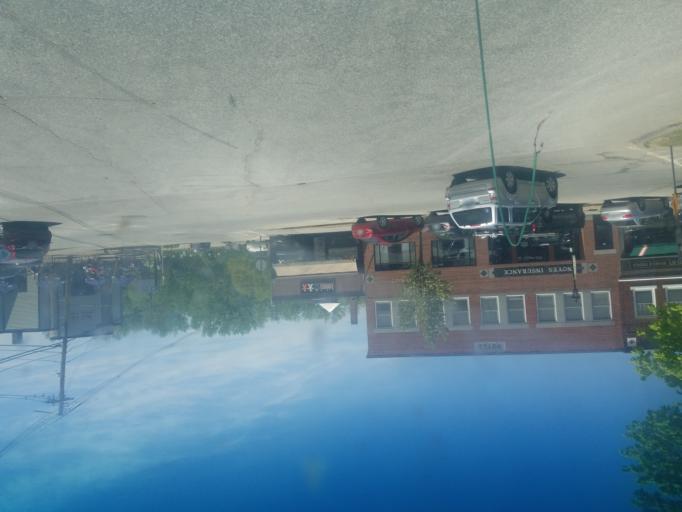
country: US
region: New Hampshire
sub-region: Grafton County
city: Plymouth
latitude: 43.7571
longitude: -71.6881
